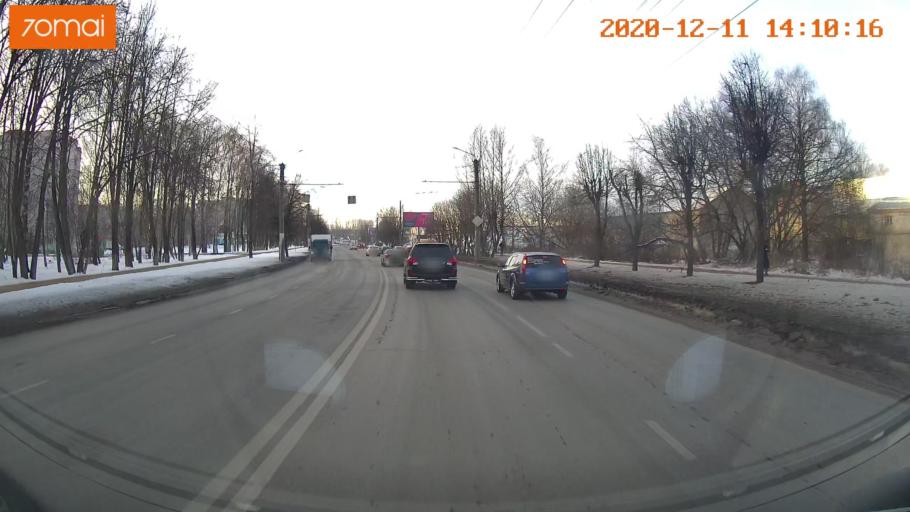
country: RU
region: Kostroma
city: Oktyabr'skiy
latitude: 57.7405
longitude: 40.9841
